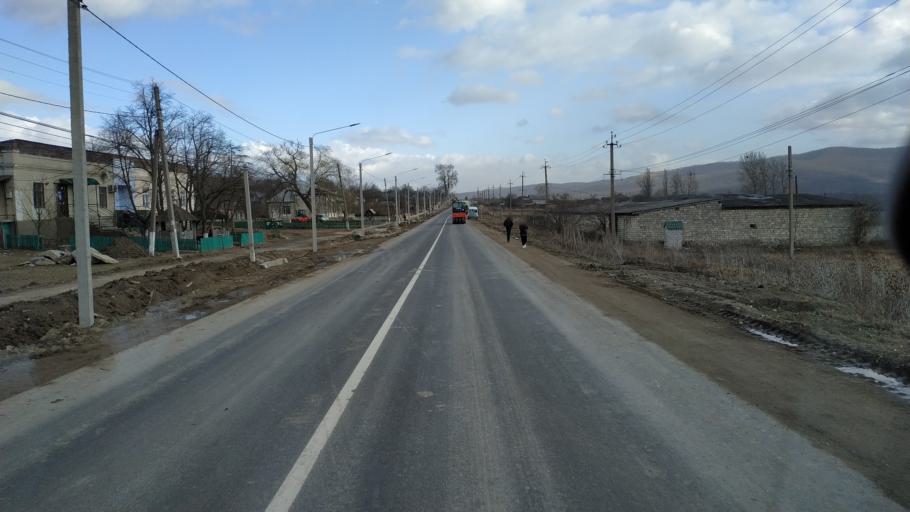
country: MD
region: Calarasi
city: Calarasi
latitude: 47.3203
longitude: 28.1097
